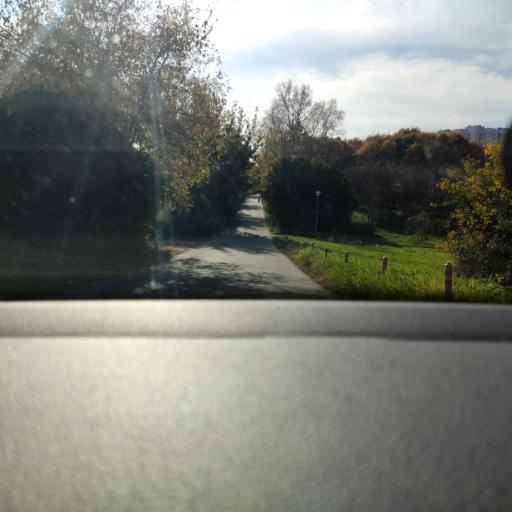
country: RU
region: Moscow
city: Orekhovo-Borisovo
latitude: 55.6282
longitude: 37.7334
